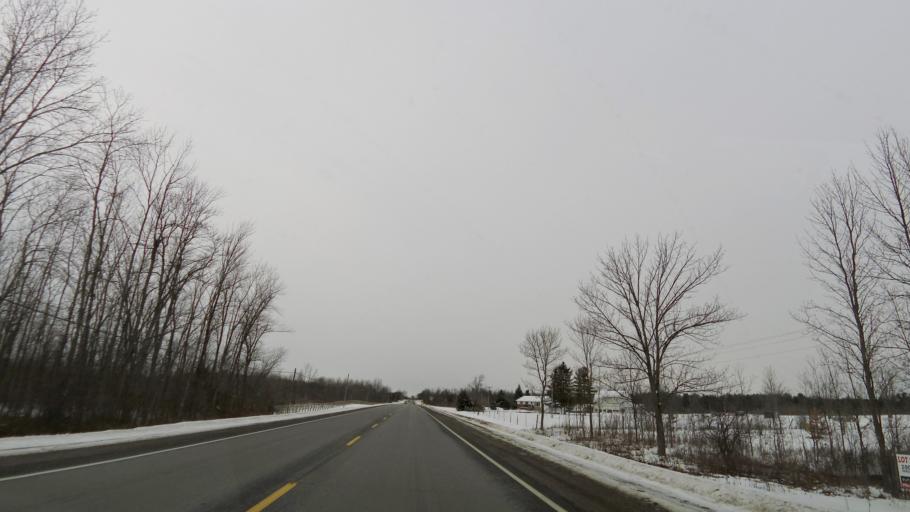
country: CA
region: Ontario
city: Cambridge
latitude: 43.3115
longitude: -80.1591
